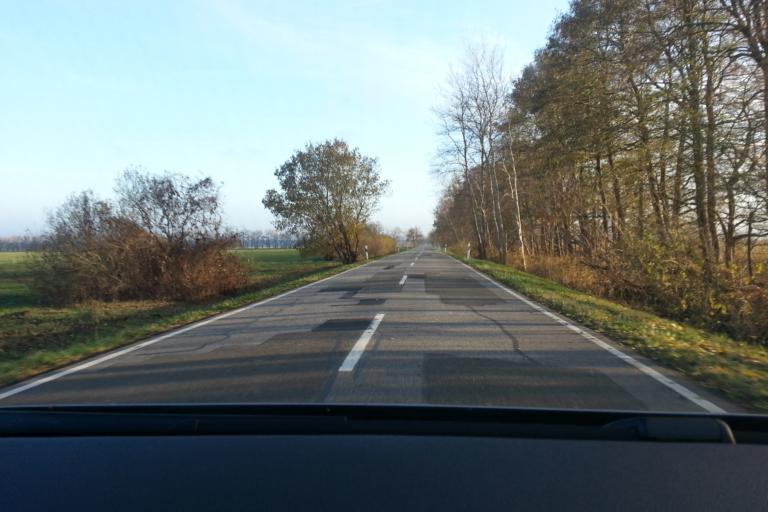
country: DE
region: Mecklenburg-Vorpommern
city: Strasburg
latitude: 53.6388
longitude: 13.7466
